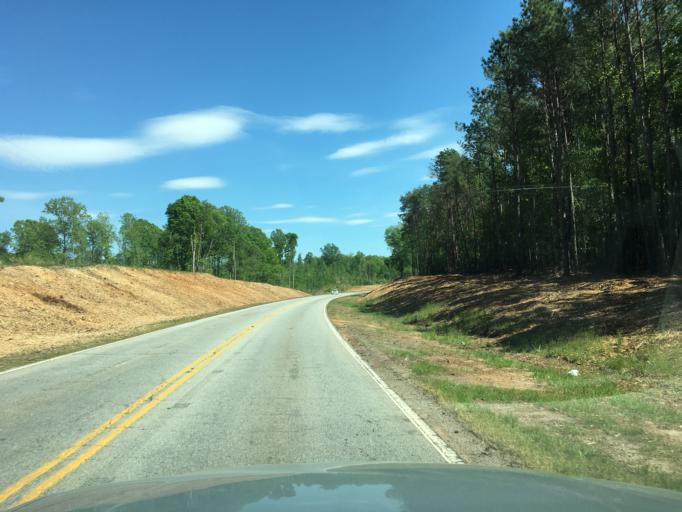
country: US
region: South Carolina
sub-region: Spartanburg County
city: Wellford
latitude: 34.9689
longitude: -82.0914
